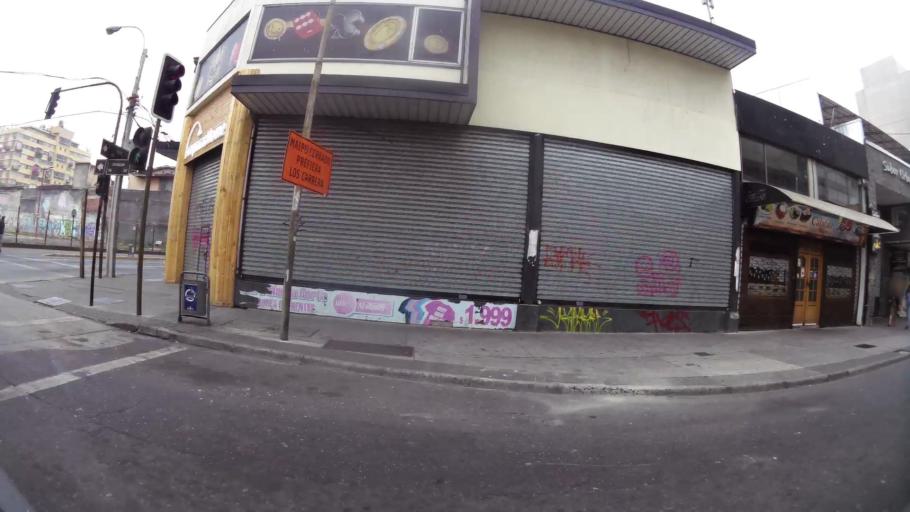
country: CL
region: Biobio
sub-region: Provincia de Concepcion
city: Concepcion
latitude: -36.8259
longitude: -73.0518
